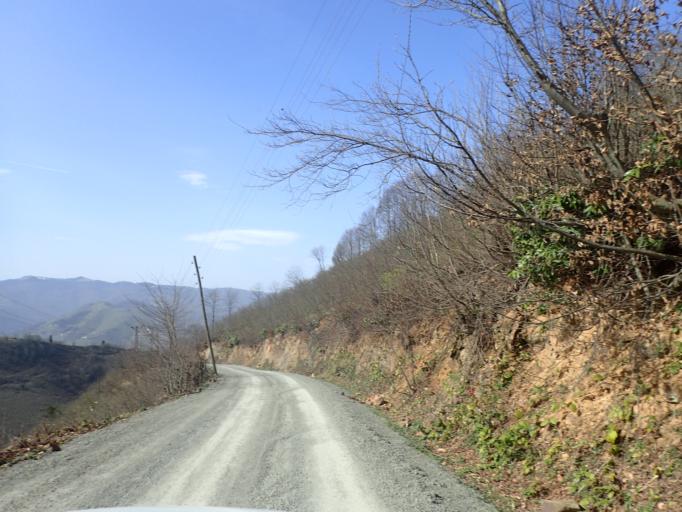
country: TR
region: Ordu
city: Kabaduz
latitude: 40.8235
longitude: 37.8899
